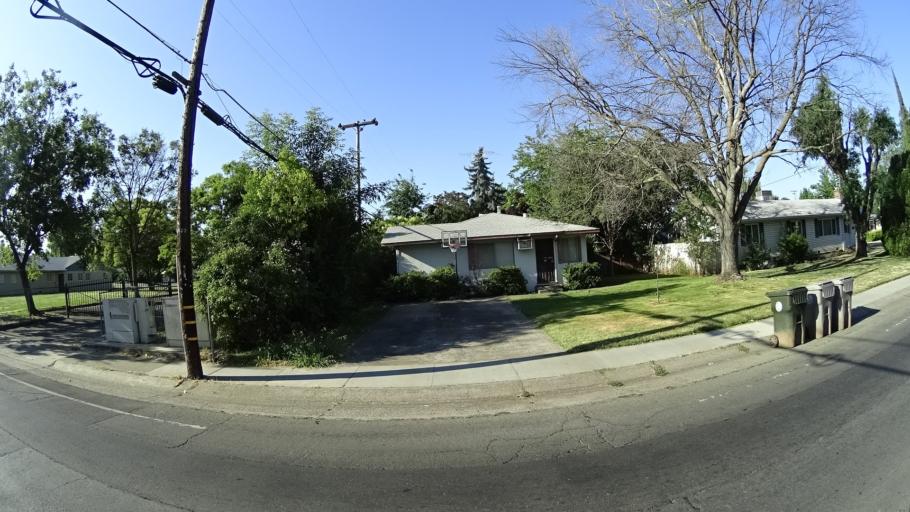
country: US
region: California
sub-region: Sacramento County
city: Florin
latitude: 38.5396
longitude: -121.4325
